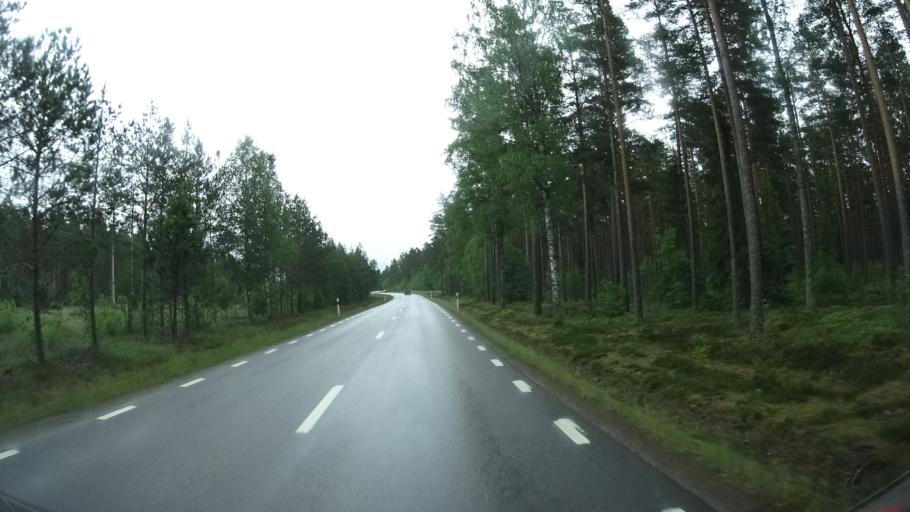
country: SE
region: Kalmar
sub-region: Hultsfreds Kommun
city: Hultsfred
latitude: 57.5138
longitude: 15.8244
